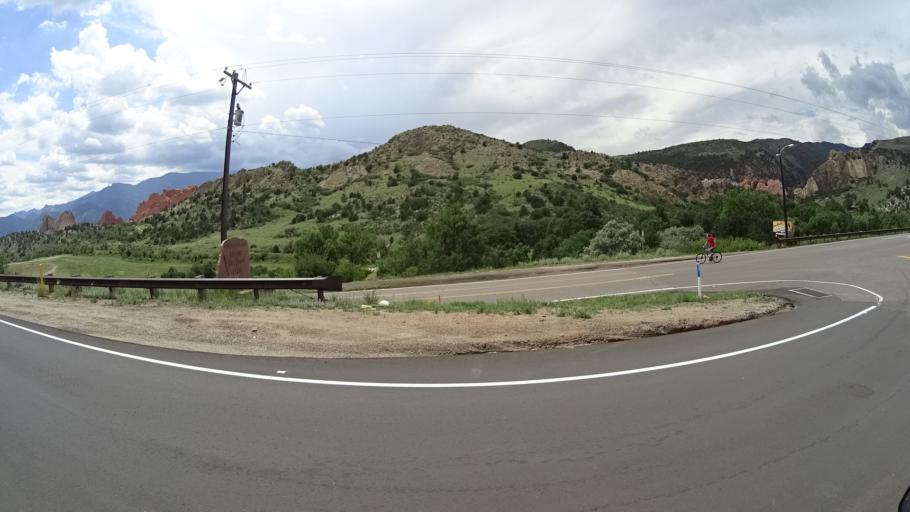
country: US
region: Colorado
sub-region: El Paso County
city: Manitou Springs
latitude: 38.8876
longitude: -104.8737
